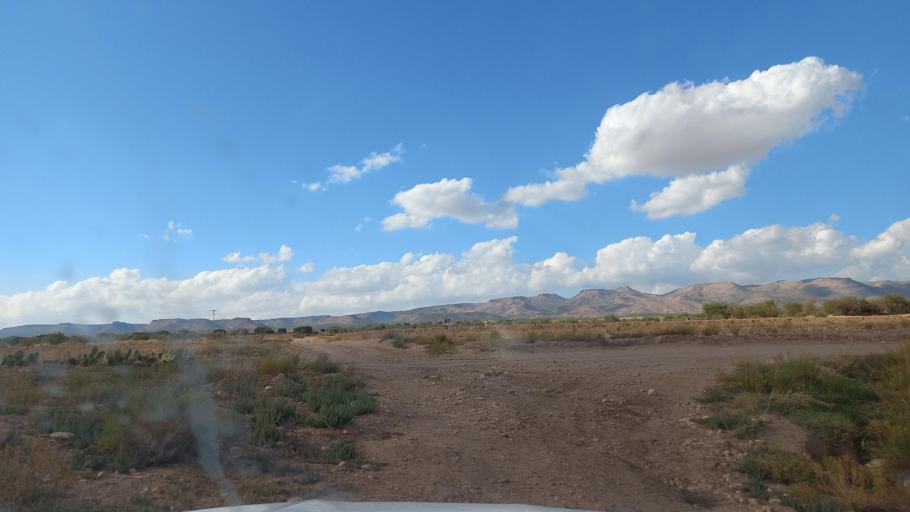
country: TN
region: Al Qasrayn
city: Sbiba
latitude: 35.3953
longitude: 9.0341
